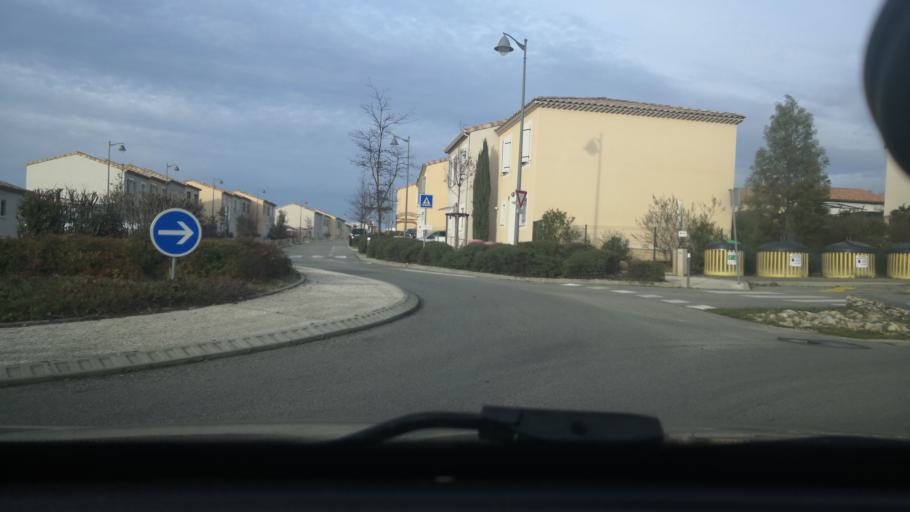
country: FR
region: Rhone-Alpes
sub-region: Departement de la Drome
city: Montelimar
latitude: 44.5369
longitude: 4.7685
